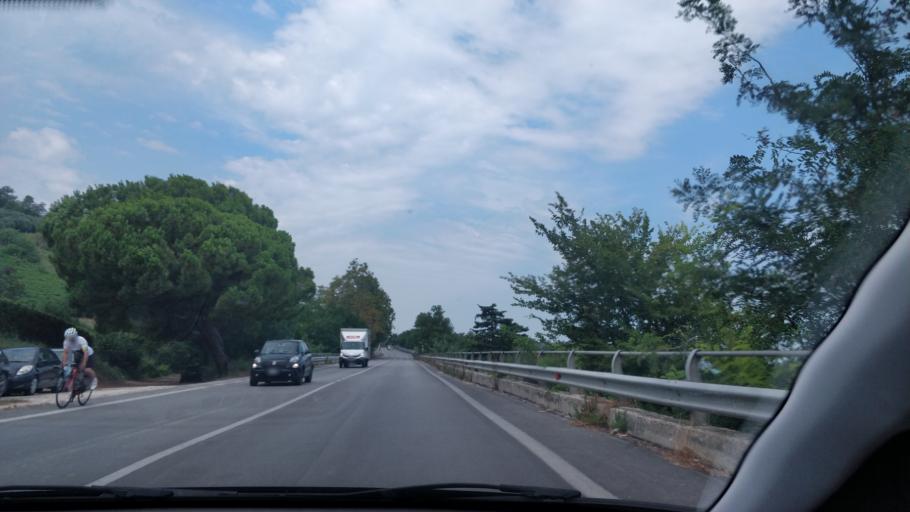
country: IT
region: Abruzzo
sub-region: Provincia di Chieti
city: Marina di San Vito
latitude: 42.3169
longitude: 14.4353
